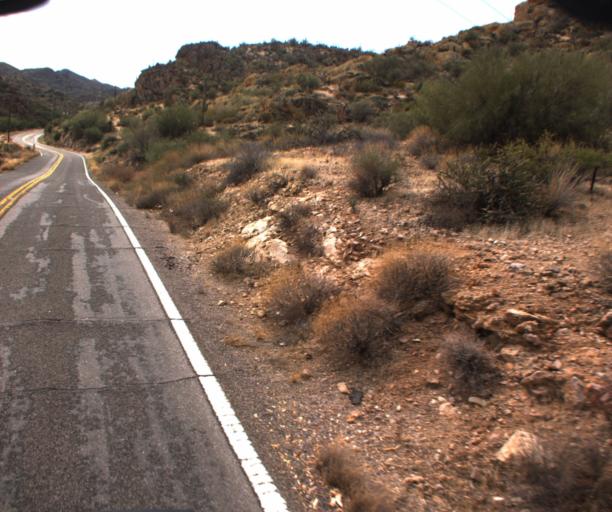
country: US
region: Arizona
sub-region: Pinal County
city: Apache Junction
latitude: 33.5334
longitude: -111.4547
